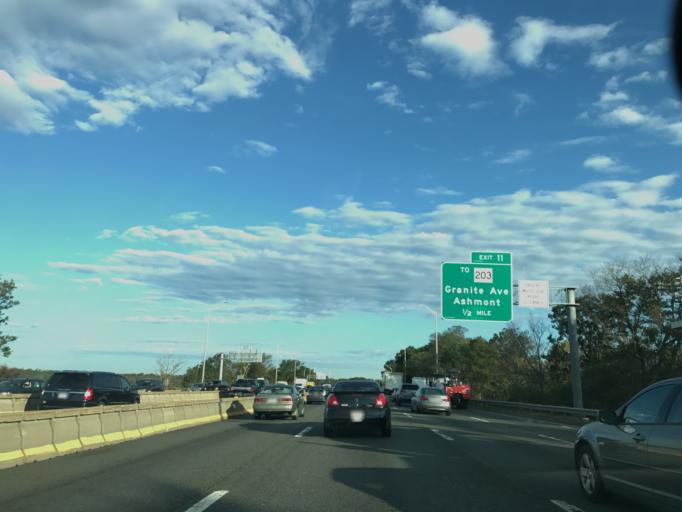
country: US
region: Massachusetts
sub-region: Norfolk County
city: Milton
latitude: 42.2678
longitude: -71.0477
